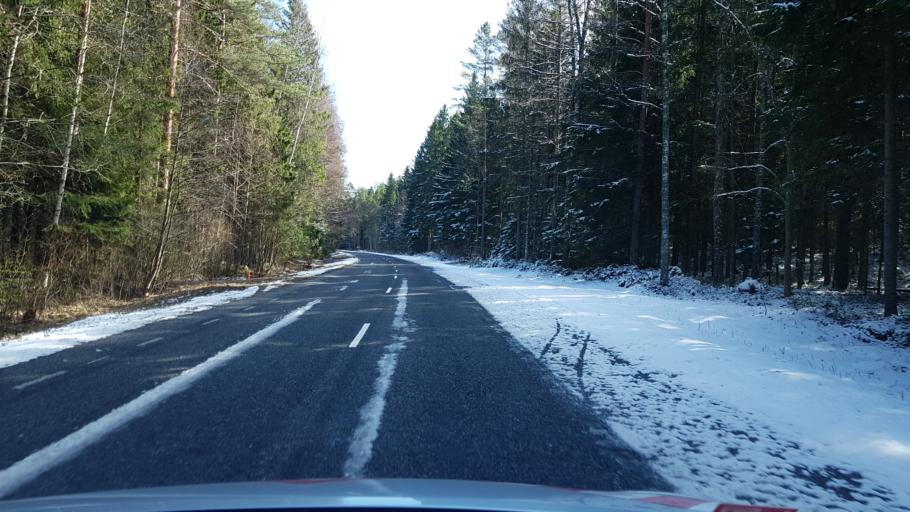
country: EE
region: Harju
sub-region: Loksa linn
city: Loksa
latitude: 59.5623
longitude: 25.9661
